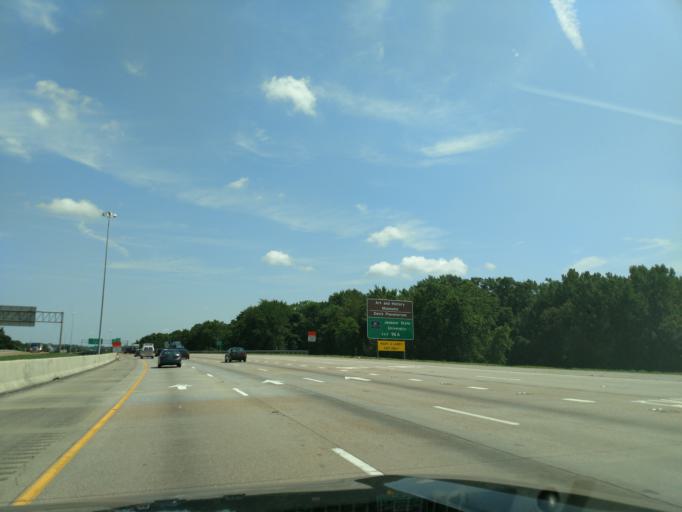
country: US
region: Mississippi
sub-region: Hinds County
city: Jackson
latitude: 32.2890
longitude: -90.1676
